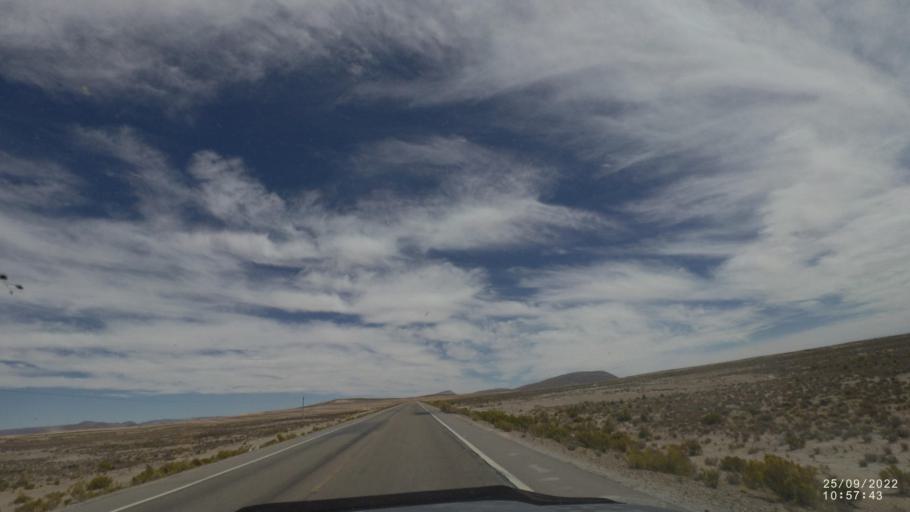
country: BO
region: Oruro
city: Challapata
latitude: -19.4721
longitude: -66.8956
